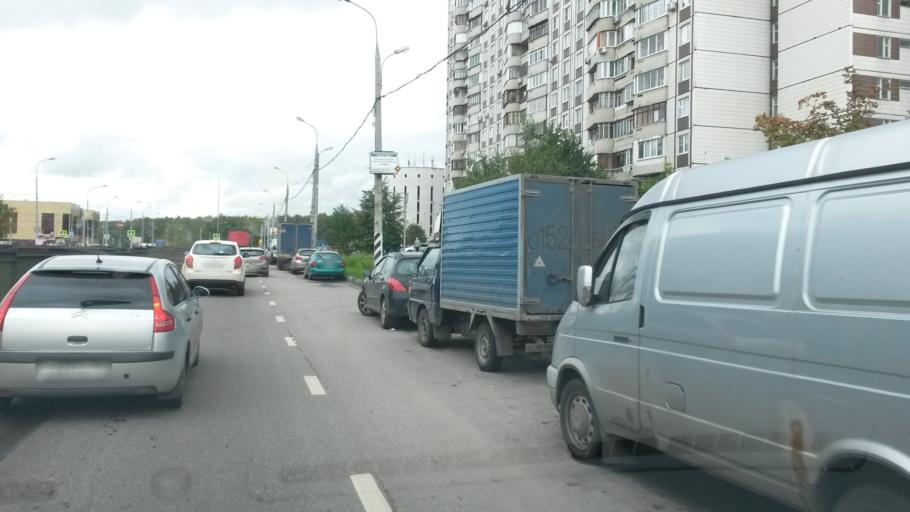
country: RU
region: Moskovskaya
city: Shcherbinka
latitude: 55.5480
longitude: 37.5447
